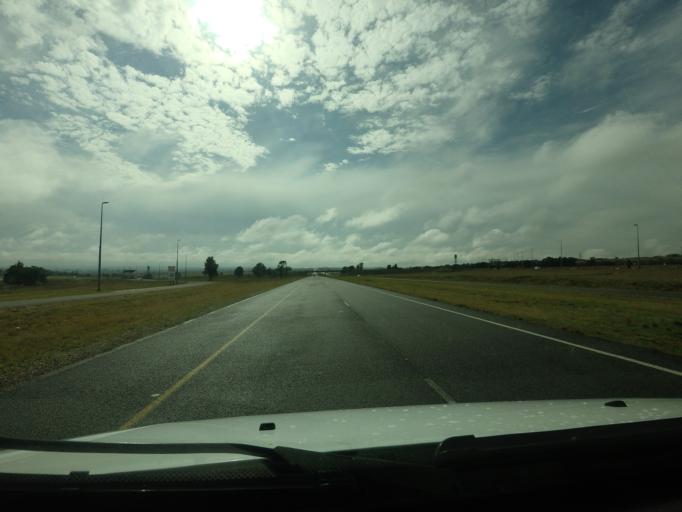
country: ZA
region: Gauteng
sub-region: City of Tshwane Metropolitan Municipality
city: Cullinan
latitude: -25.7973
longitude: 28.5134
